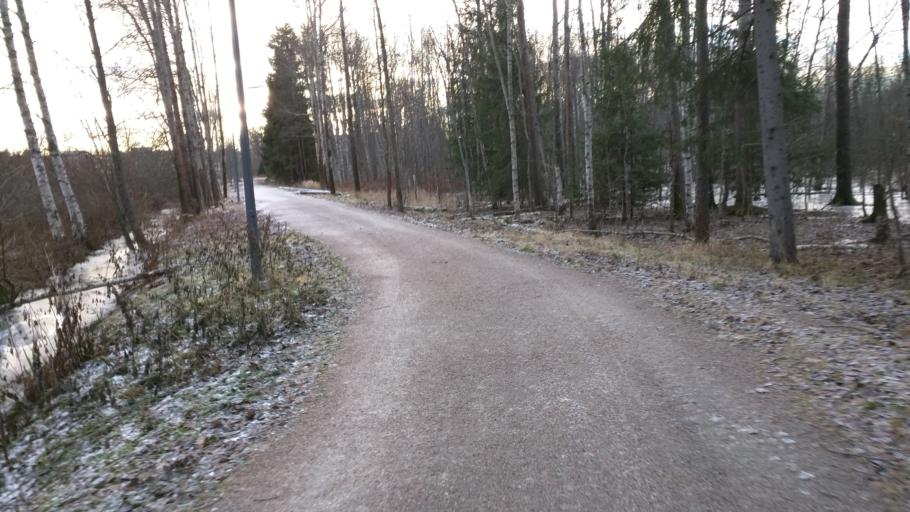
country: FI
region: Uusimaa
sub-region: Helsinki
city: Kauniainen
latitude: 60.2428
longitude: 24.7344
